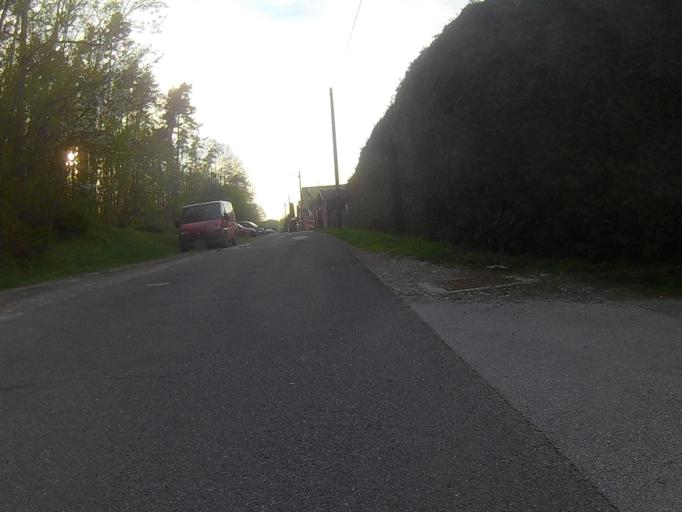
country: SI
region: Maribor
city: Pekre
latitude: 46.5368
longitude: 15.5913
